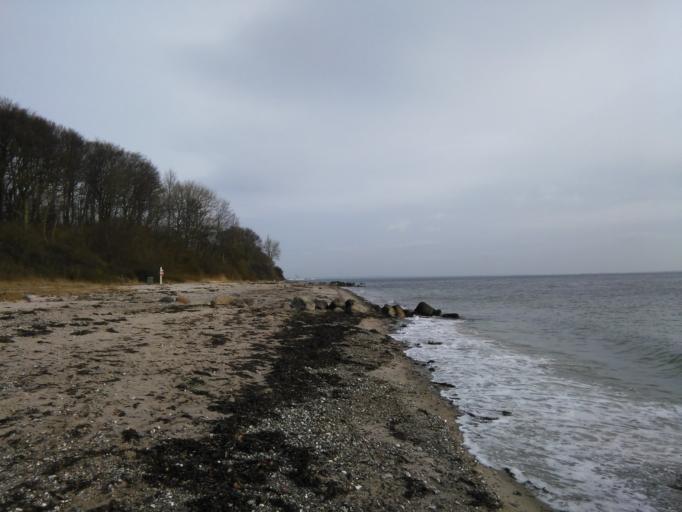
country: DK
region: Central Jutland
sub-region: Arhus Kommune
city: Beder
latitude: 56.0900
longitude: 10.2488
